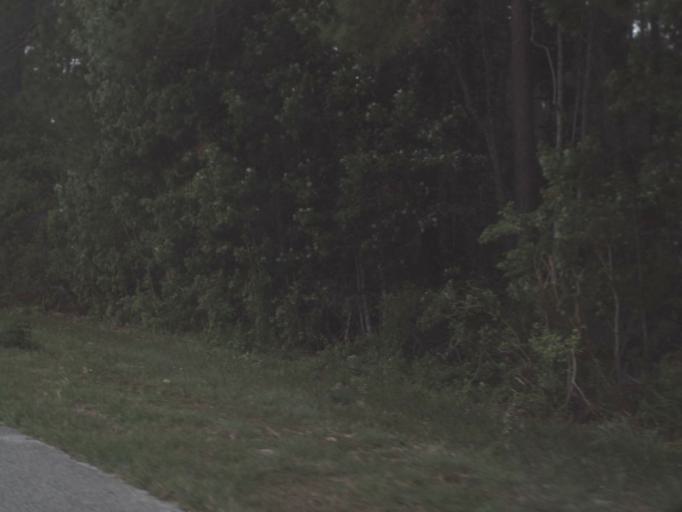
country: US
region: Florida
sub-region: Lake County
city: Lake Mack-Forest Hills
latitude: 28.9774
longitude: -81.4048
